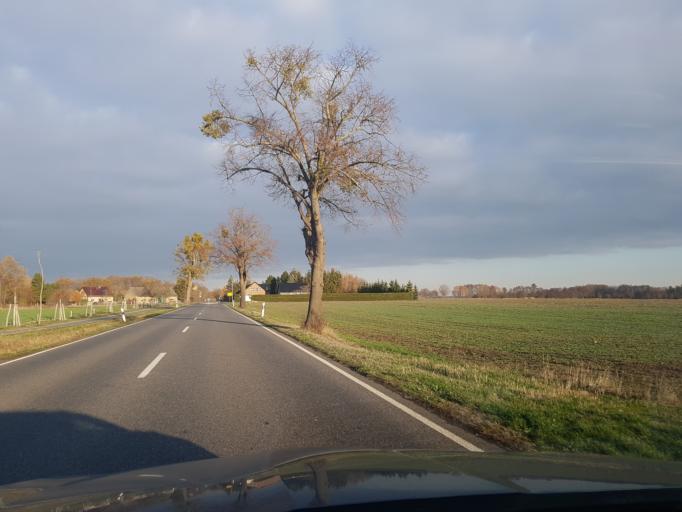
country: DE
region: Brandenburg
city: Luckau
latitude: 51.8694
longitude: 13.7000
